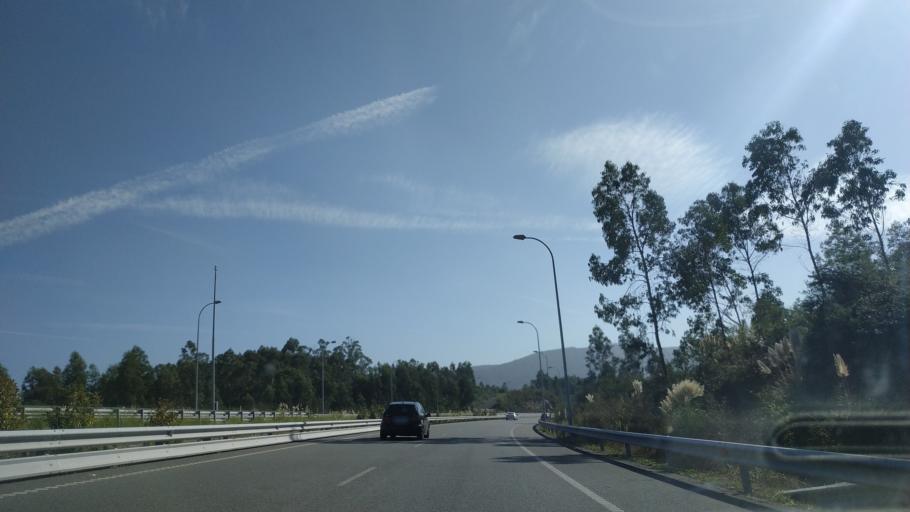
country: ES
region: Galicia
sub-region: Provincia da Coruna
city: Culleredo
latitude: 43.2811
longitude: -8.3941
